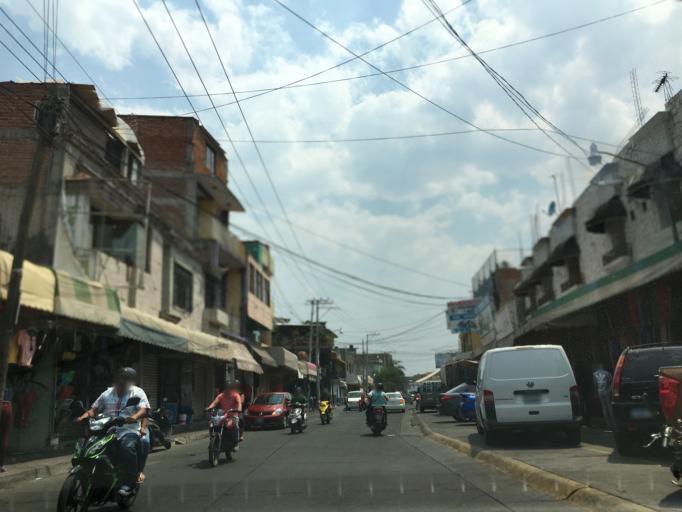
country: MX
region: Guanajuato
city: Uriangato
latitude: 20.1346
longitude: -101.1849
